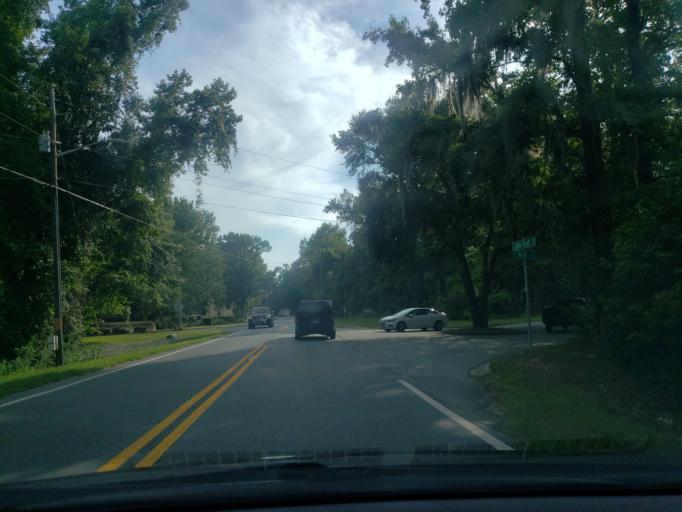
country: US
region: Georgia
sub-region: Chatham County
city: Montgomery
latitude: 31.9587
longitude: -81.1403
